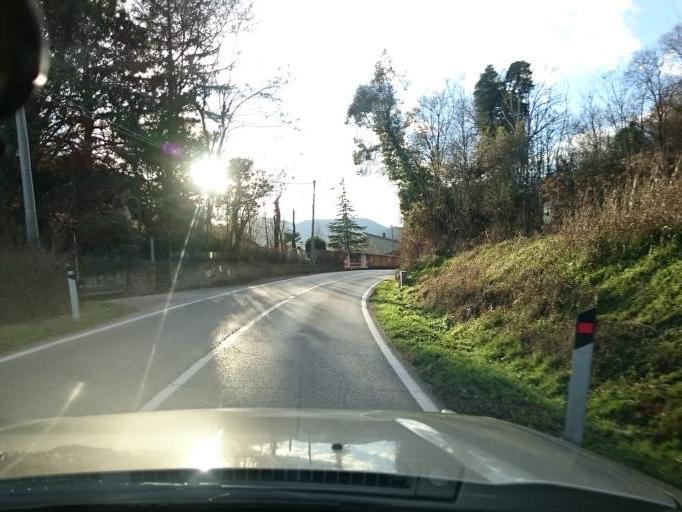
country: IT
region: Veneto
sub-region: Provincia di Padova
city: Torreglia
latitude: 45.3424
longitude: 11.7367
